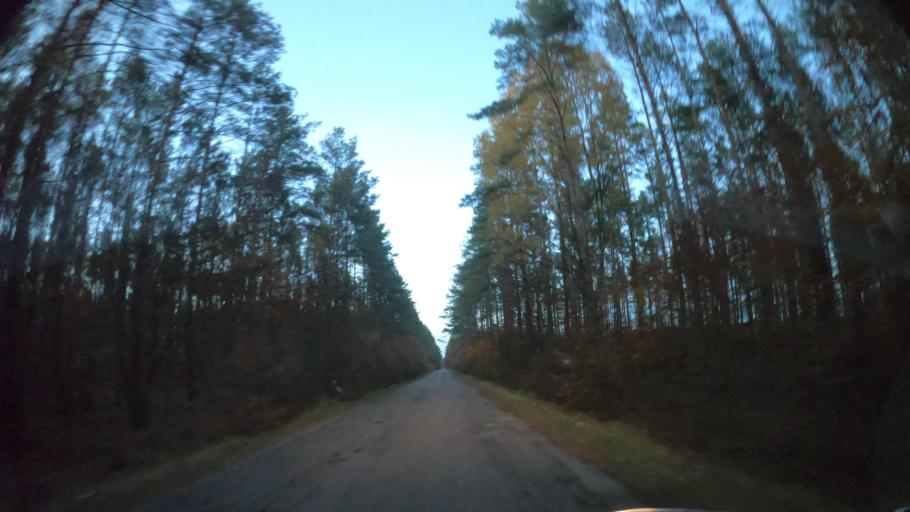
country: PL
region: Greater Poland Voivodeship
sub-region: Powiat zlotowski
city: Sypniewo
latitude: 53.4121
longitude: 16.5877
